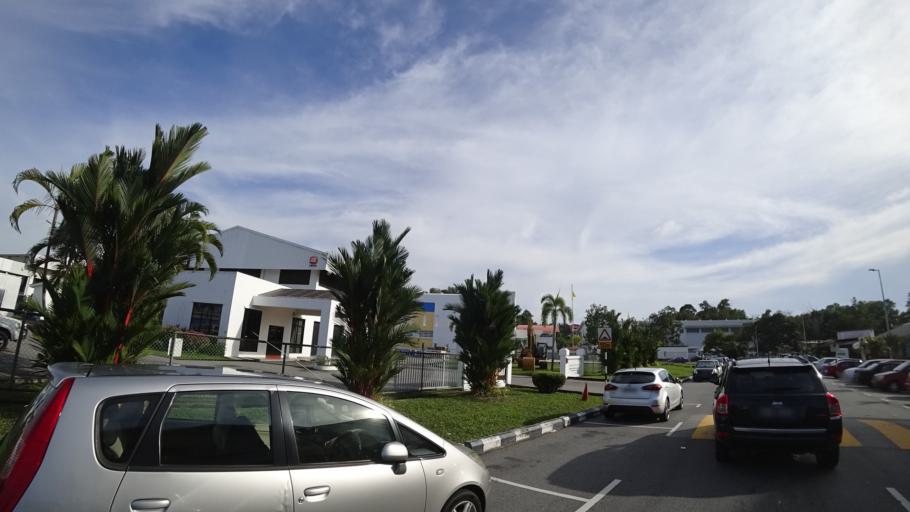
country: BN
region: Brunei and Muara
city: Bandar Seri Begawan
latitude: 4.8928
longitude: 114.9026
